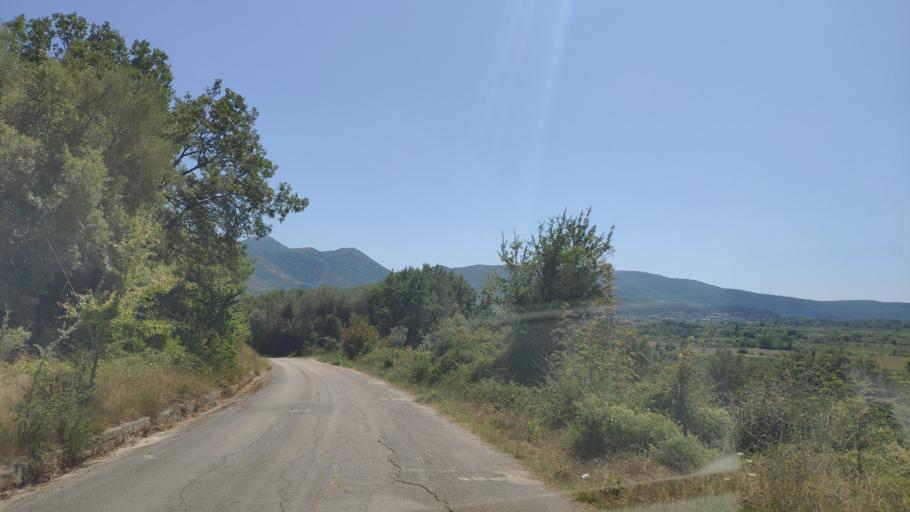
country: GR
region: Epirus
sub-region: Nomos Prevezis
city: Kanalaki
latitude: 39.2697
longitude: 20.6005
